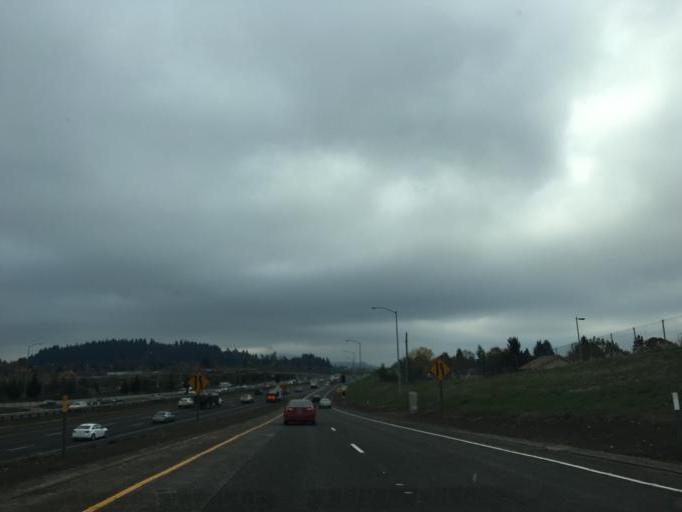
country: US
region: Oregon
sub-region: Multnomah County
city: Lents
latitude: 45.5176
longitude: -122.5660
